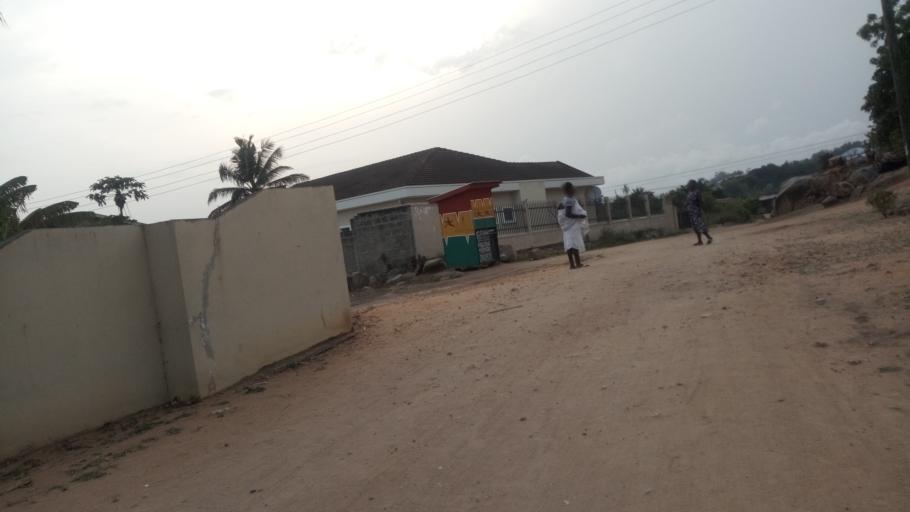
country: GH
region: Central
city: Winneba
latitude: 5.3567
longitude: -0.6236
